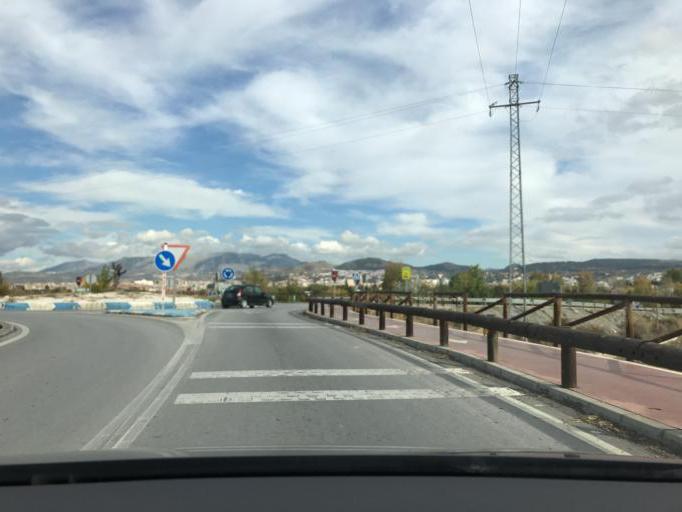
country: ES
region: Andalusia
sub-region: Provincia de Granada
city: Armilla
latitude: 37.1627
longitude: -3.6283
